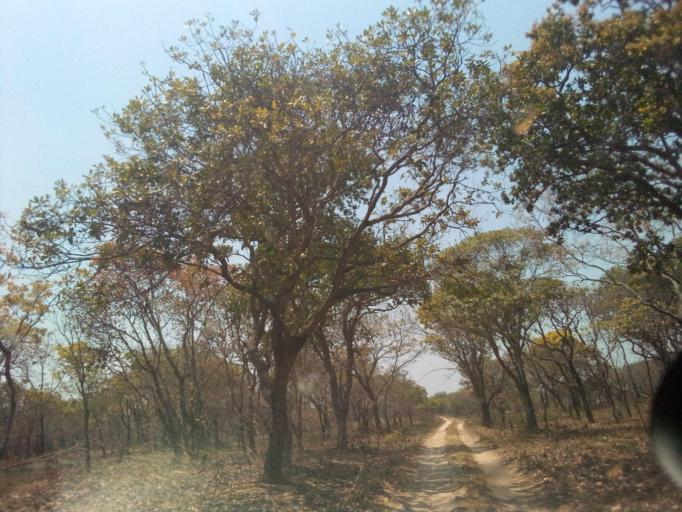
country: ZM
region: Copperbelt
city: Kataba
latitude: -12.2405
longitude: 30.4026
